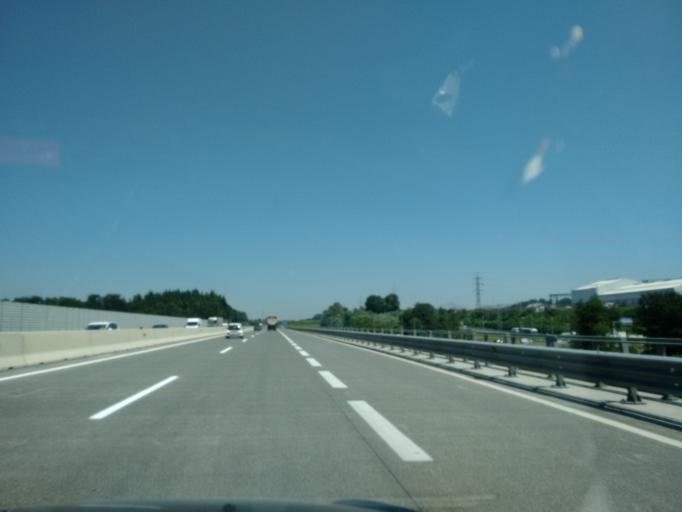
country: AT
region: Upper Austria
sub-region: Politischer Bezirk Gmunden
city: Laakirchen
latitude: 47.9968
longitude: 13.7949
